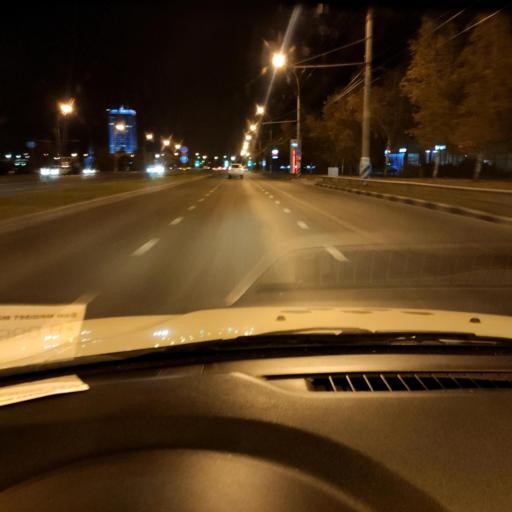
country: RU
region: Samara
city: Tol'yatti
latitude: 53.5471
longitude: 49.2658
